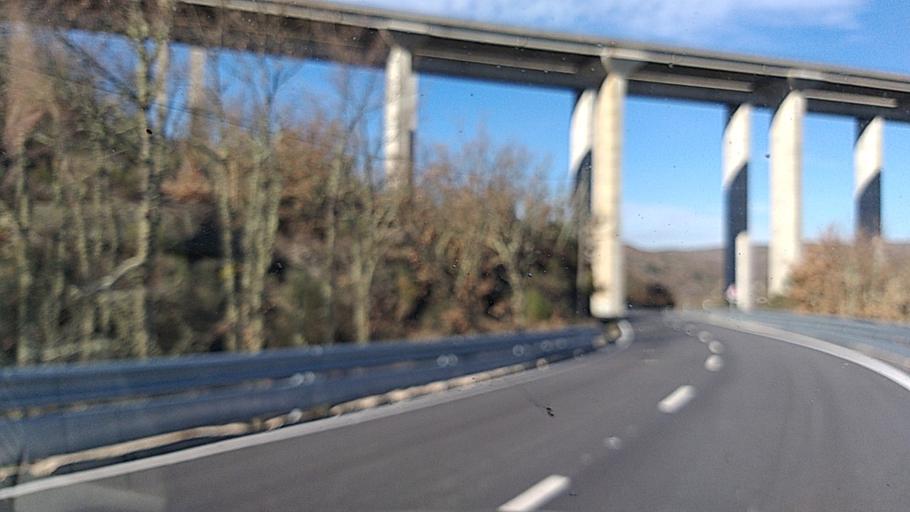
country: ES
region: Castille and Leon
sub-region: Provincia de Salamanca
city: Fuentes de Onoro
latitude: 40.6092
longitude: -6.9221
